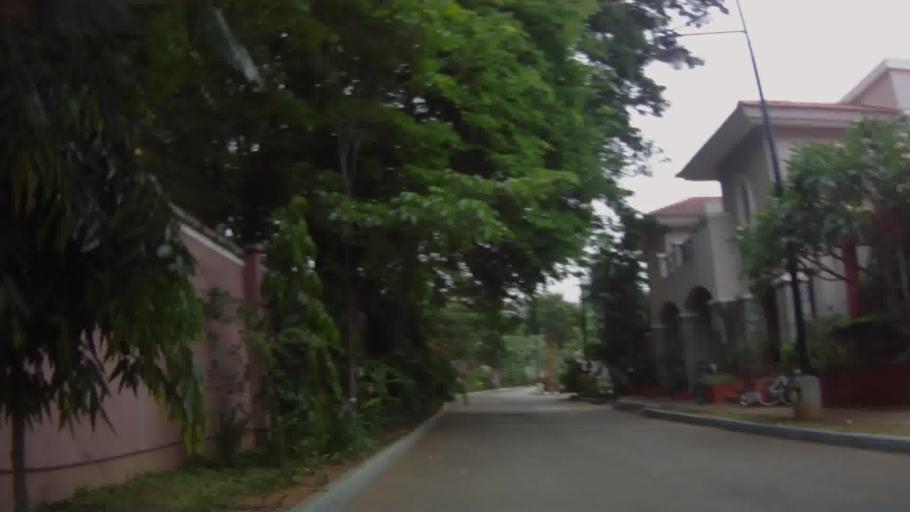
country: IN
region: Karnataka
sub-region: Bangalore Rural
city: Hoskote
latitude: 12.9594
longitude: 77.7489
